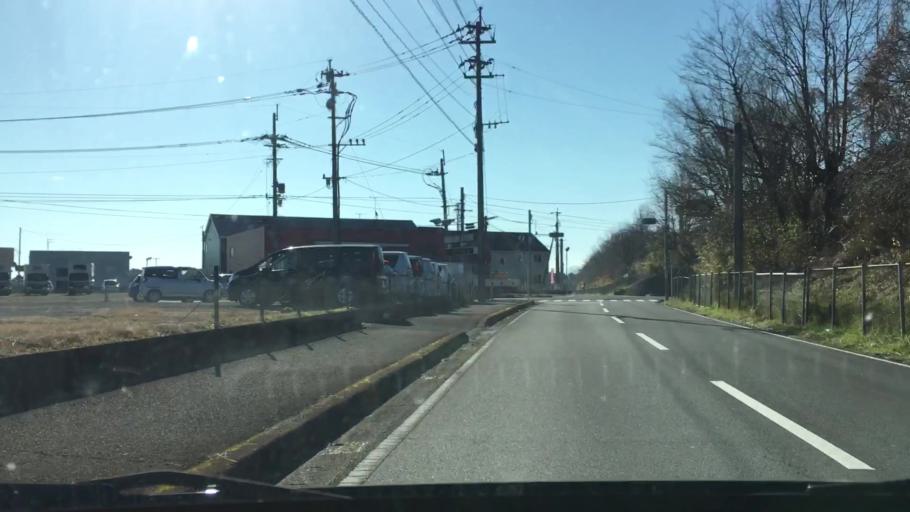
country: JP
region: Kagoshima
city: Kajiki
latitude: 31.7941
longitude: 130.7166
